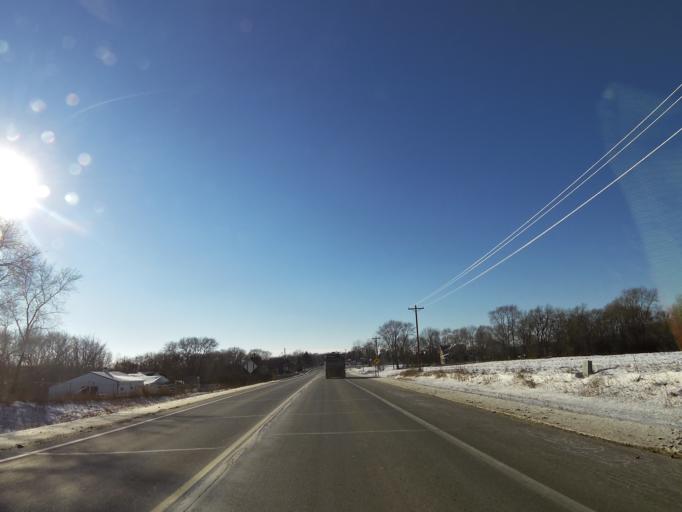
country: US
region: Minnesota
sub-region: Scott County
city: Shakopee
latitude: 44.8070
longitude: -93.5621
